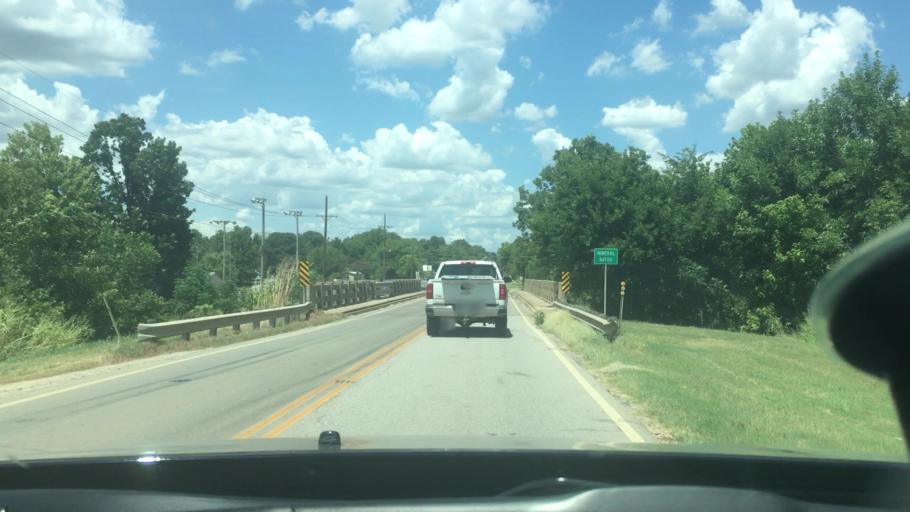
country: US
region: Oklahoma
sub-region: Bryan County
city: Durant
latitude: 33.9841
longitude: -96.3712
